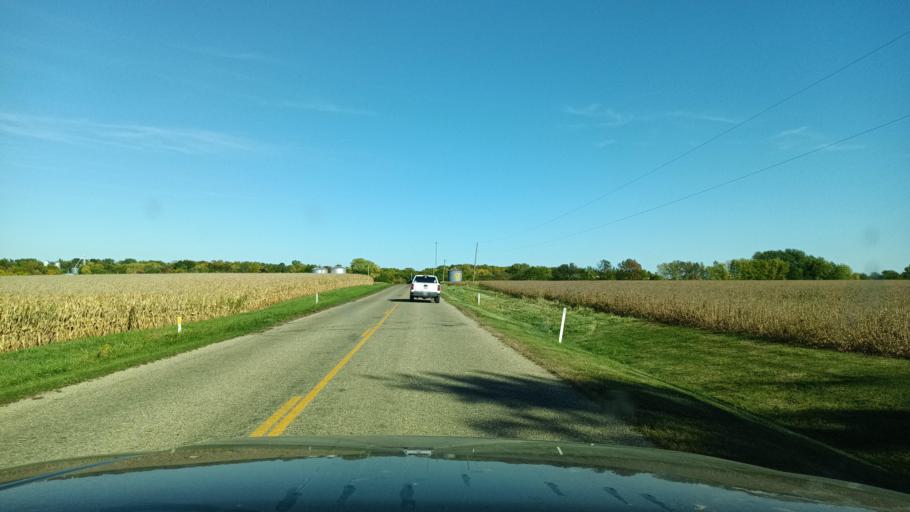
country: US
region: Illinois
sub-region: Logan County
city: Atlanta
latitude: 40.2344
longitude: -89.1375
